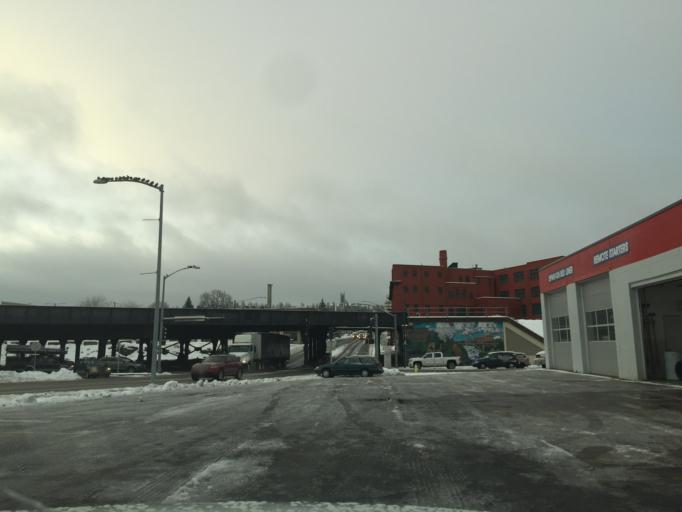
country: US
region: Washington
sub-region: Spokane County
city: Spokane
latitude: 47.6579
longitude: -117.4113
